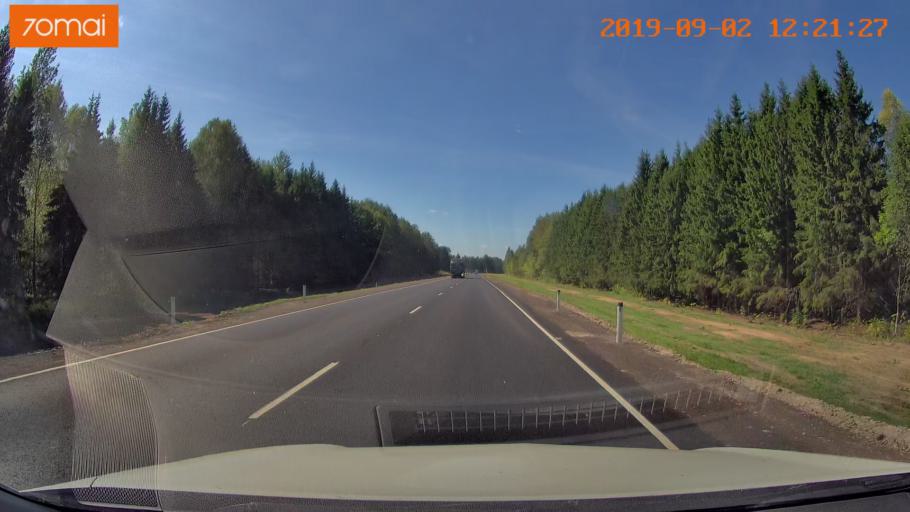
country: RU
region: Smolensk
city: Oster
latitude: 53.8875
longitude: 32.6555
